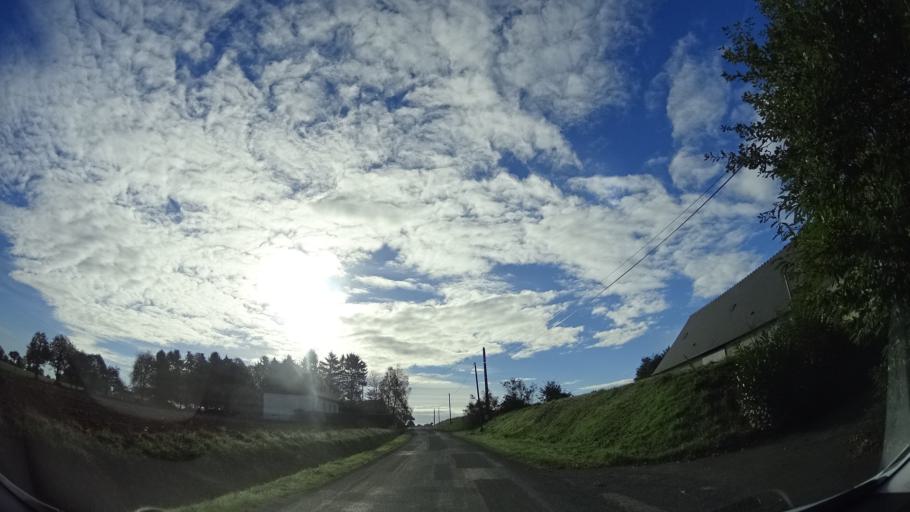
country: FR
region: Brittany
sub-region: Departement d'Ille-et-Vilaine
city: Geveze
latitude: 48.1935
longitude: -1.8180
